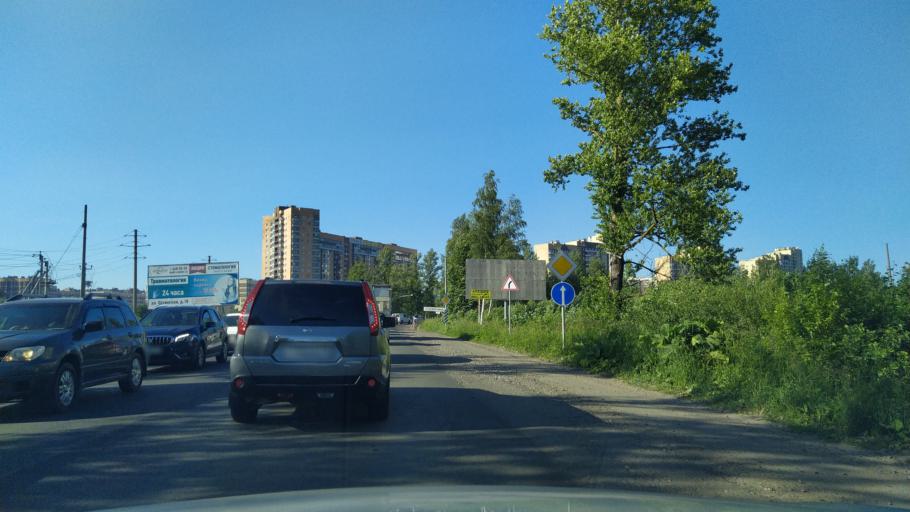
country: RU
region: Leningrad
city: Murino
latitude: 60.0525
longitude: 30.4657
